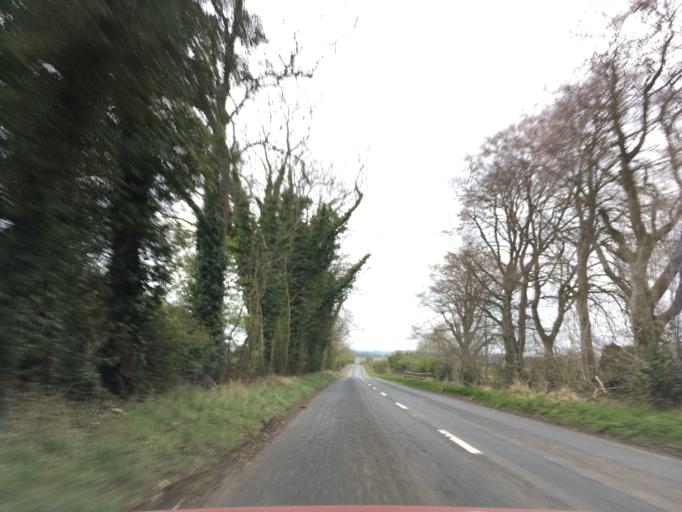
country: GB
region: England
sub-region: Gloucestershire
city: Bourton on the Water
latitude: 51.7893
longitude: -1.7414
